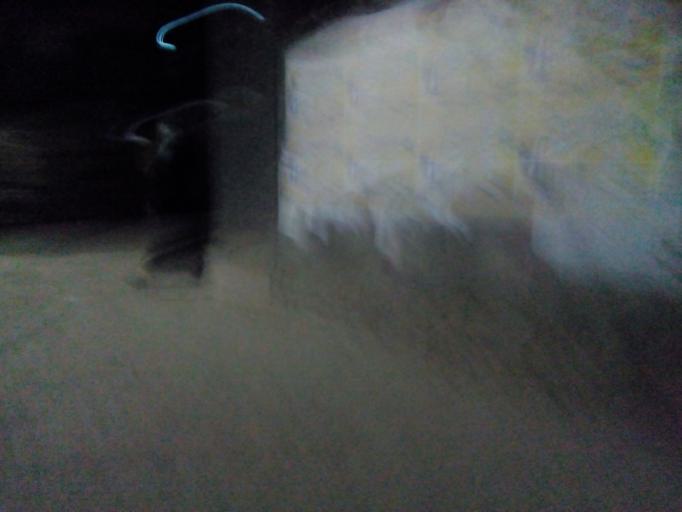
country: BD
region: Dhaka
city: Paltan
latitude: 23.7453
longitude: 90.4213
